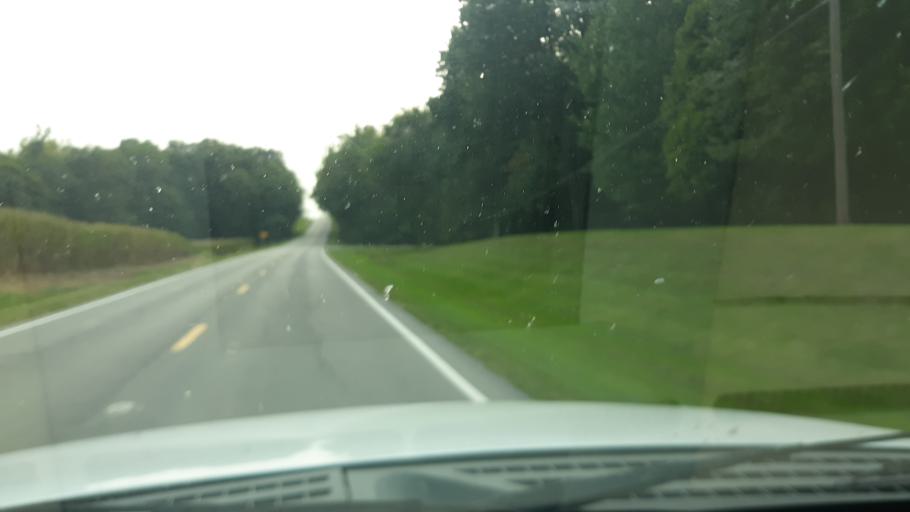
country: US
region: Illinois
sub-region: Wabash County
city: Mount Carmel
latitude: 38.3851
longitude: -87.8201
